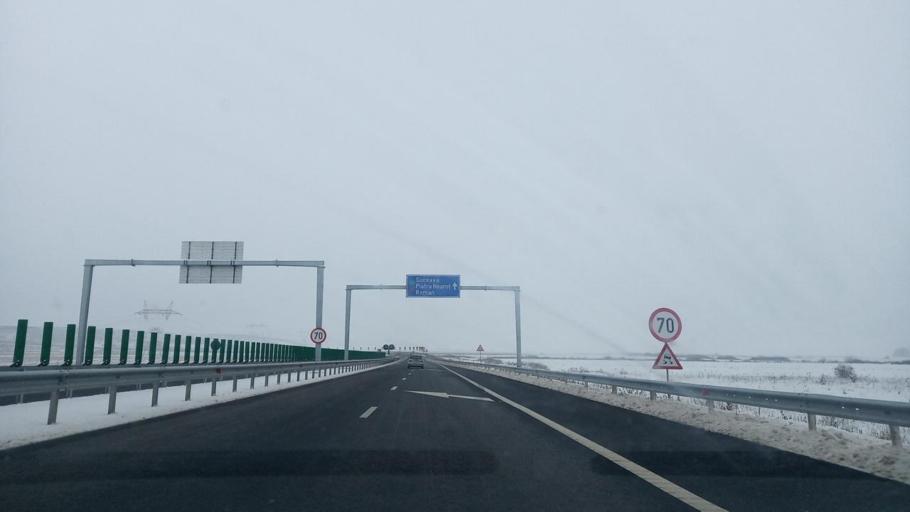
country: RO
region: Bacau
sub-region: Comuna Saucesti
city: Saucesti
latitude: 46.6345
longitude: 26.9350
